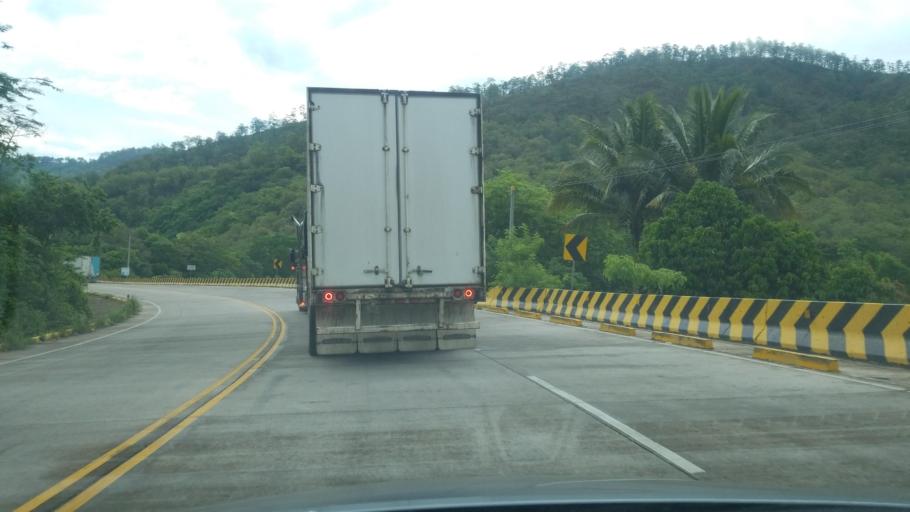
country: HN
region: Copan
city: Copan
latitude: 14.8569
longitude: -89.2183
